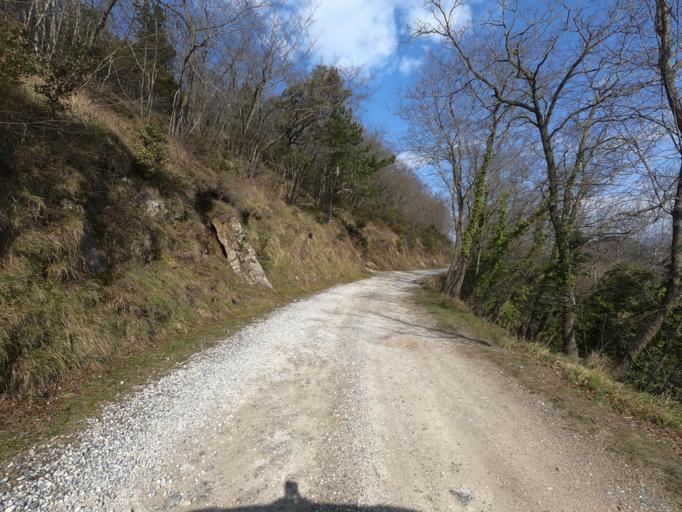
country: IT
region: Liguria
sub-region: Provincia di Savona
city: Balestrino
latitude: 44.1135
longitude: 8.1485
